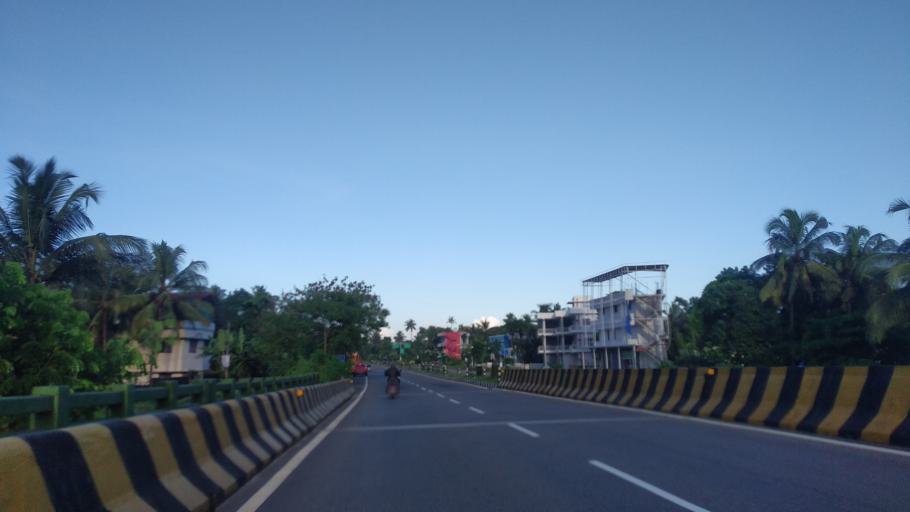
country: IN
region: Kerala
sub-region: Ernakulam
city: Elur
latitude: 10.0498
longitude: 76.2748
